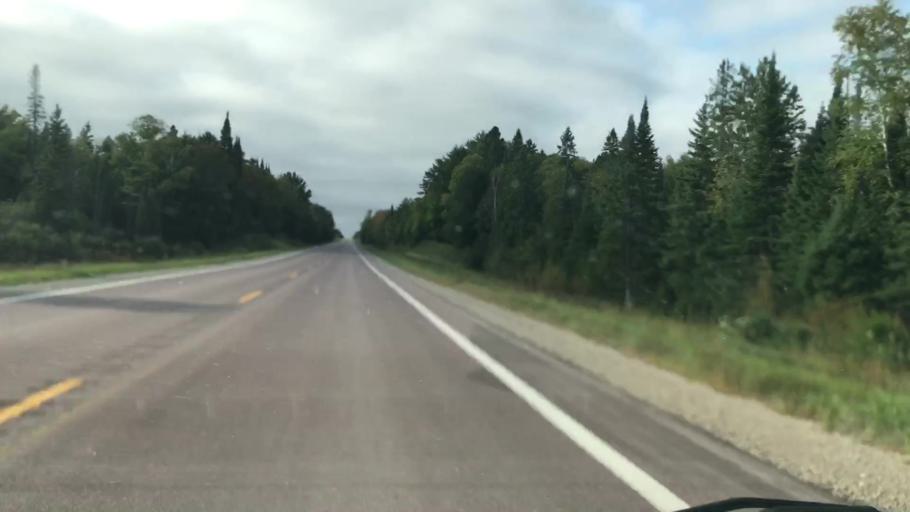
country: US
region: Michigan
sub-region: Luce County
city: Newberry
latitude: 46.2956
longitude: -85.5691
